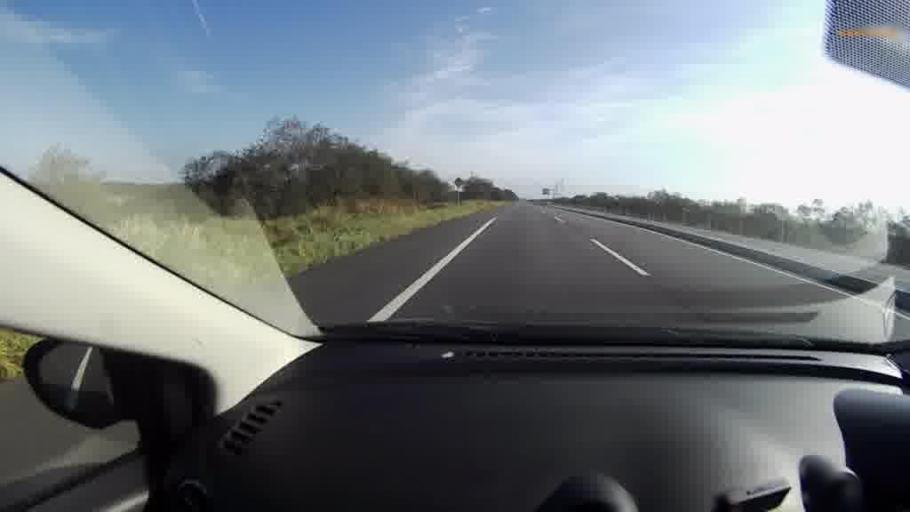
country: JP
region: Hokkaido
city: Kushiro
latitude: 43.0262
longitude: 144.2887
